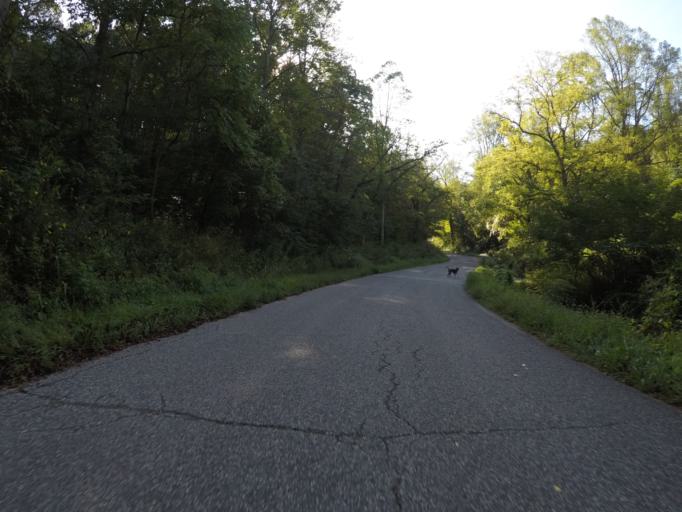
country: US
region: Kentucky
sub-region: Boyd County
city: Ashland
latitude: 38.5246
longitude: -82.5324
